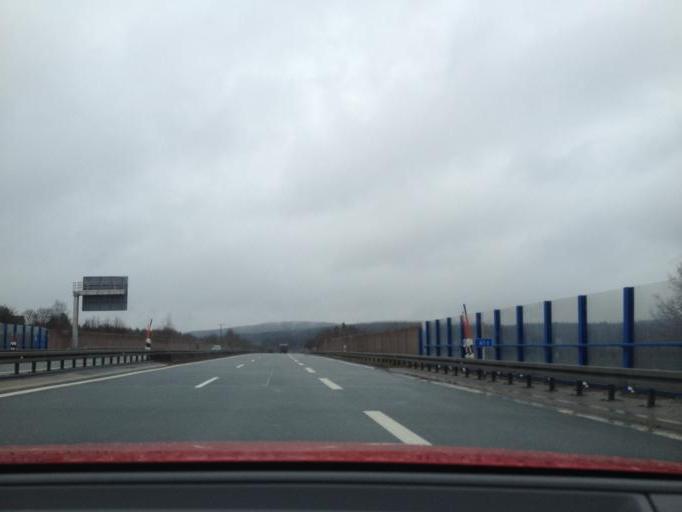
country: DE
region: Bavaria
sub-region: Upper Franconia
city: Rehau
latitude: 50.2445
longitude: 12.0612
